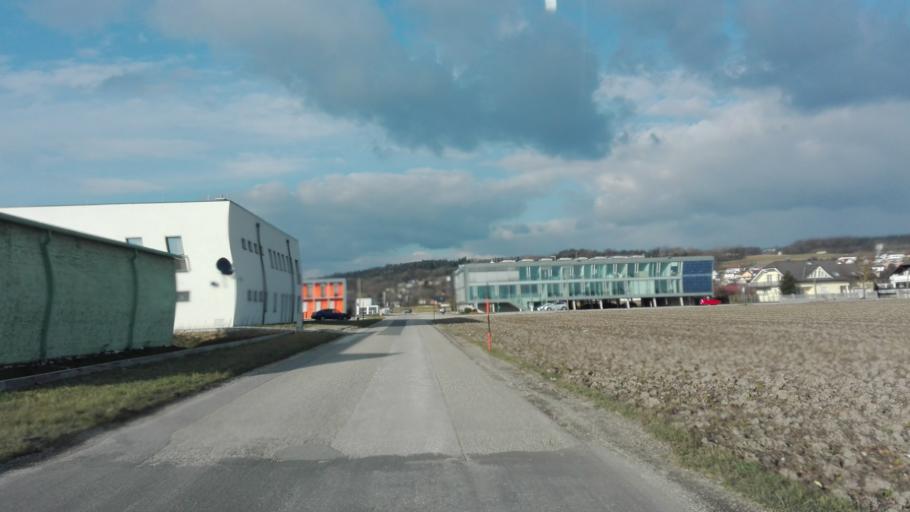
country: AT
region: Upper Austria
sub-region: Politischer Bezirk Perg
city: Perg
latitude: 48.2443
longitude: 14.6197
